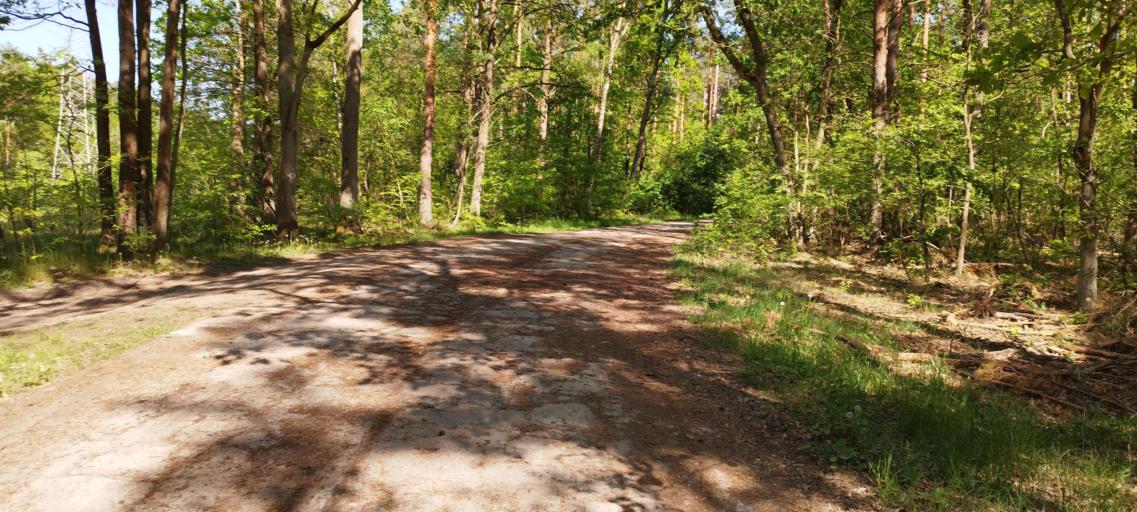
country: DE
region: Brandenburg
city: Furstenwalde
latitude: 52.3791
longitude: 14.0376
